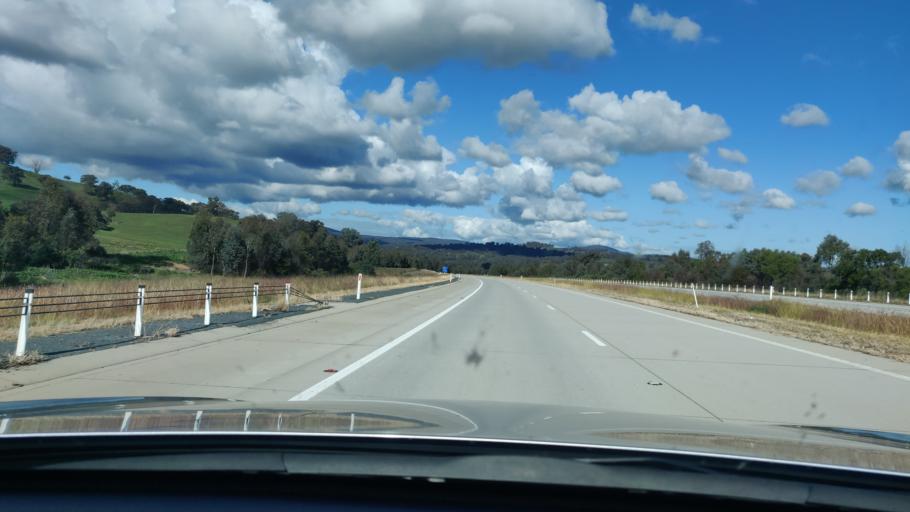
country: AU
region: New South Wales
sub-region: Greater Hume Shire
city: Holbrook
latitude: -35.8113
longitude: 147.2381
